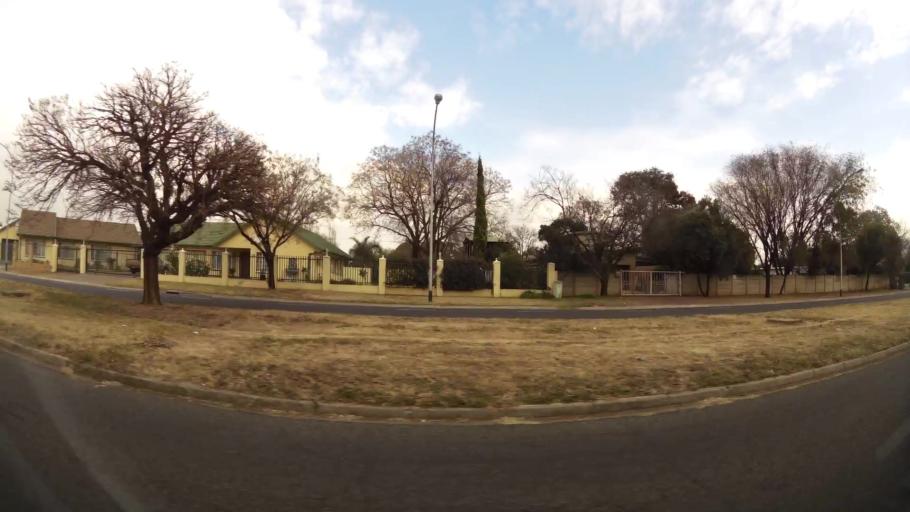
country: ZA
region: Orange Free State
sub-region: Mangaung Metropolitan Municipality
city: Bloemfontein
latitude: -29.1198
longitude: 26.1647
